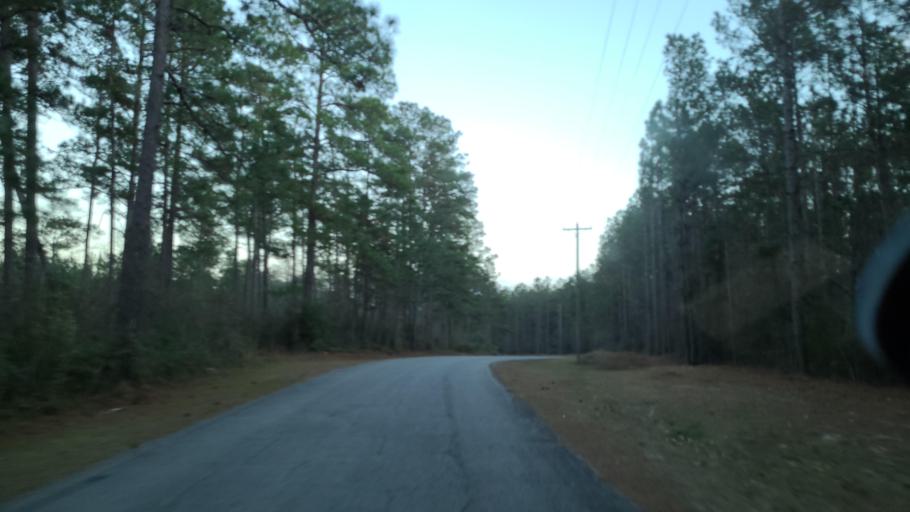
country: US
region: Mississippi
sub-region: Perry County
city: New Augusta
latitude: 31.1662
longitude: -89.2018
